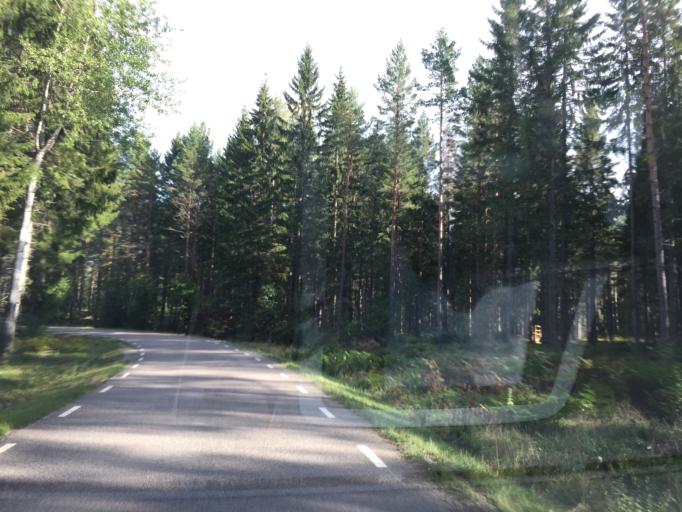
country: SE
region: Soedermanland
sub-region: Vingakers Kommun
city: Vingaker
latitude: 59.0080
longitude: 15.7251
